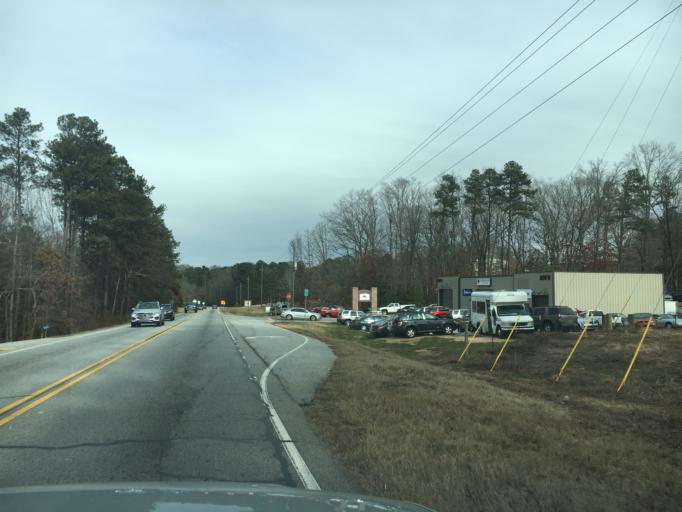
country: US
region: Georgia
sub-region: Barrow County
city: Winder
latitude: 33.9498
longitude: -83.7509
